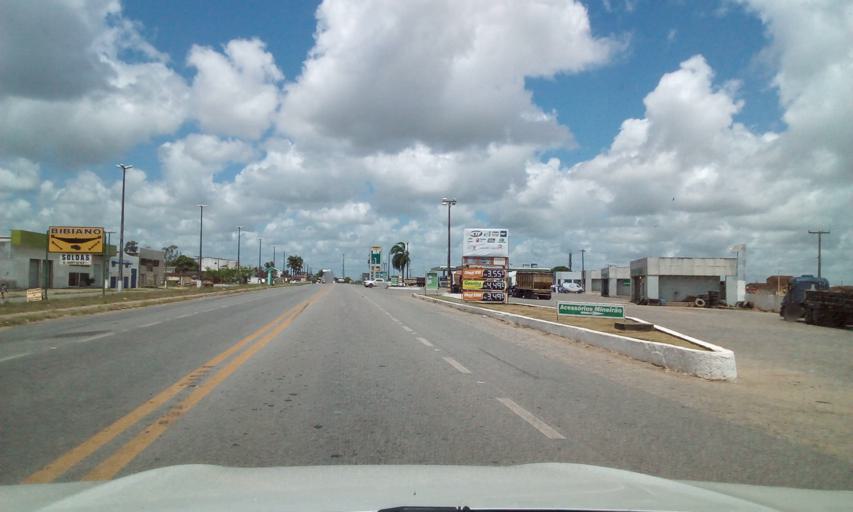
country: BR
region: Alagoas
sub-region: Sao Miguel Dos Campos
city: Sao Miguel dos Campos
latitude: -9.8019
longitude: -36.1124
